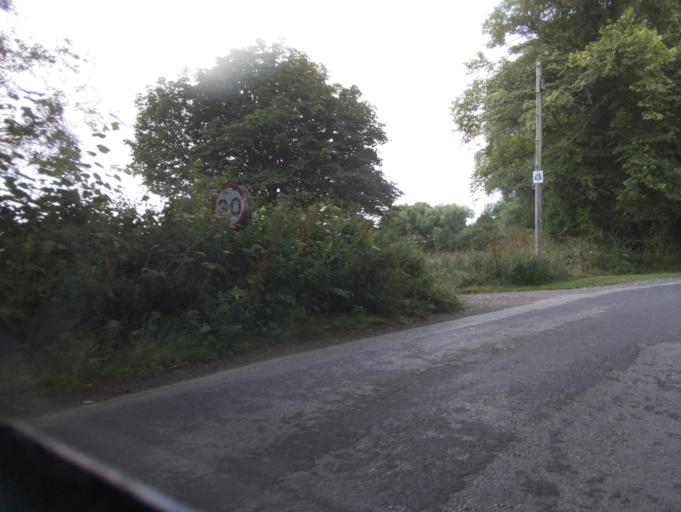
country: GB
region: England
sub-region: Wiltshire
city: Hankerton
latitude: 51.6338
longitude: -2.0640
